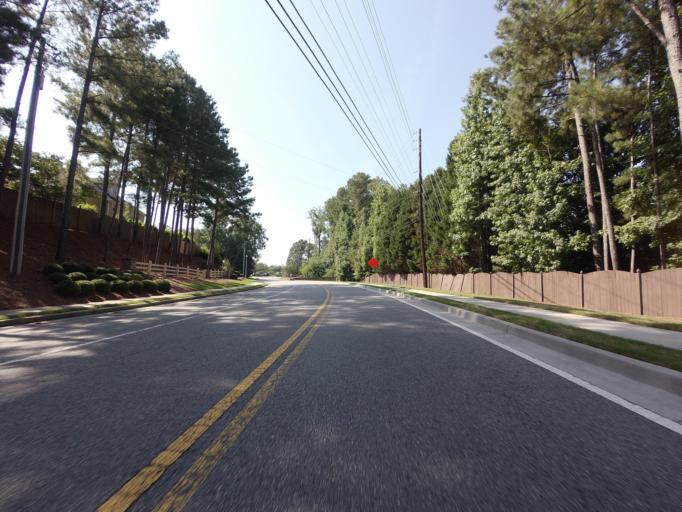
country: US
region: Georgia
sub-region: Fulton County
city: Johns Creek
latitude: 34.0734
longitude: -84.2065
